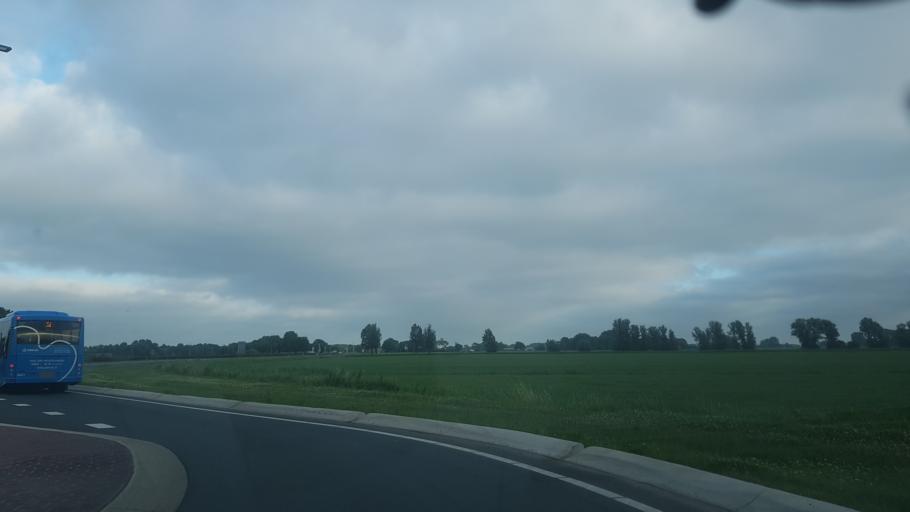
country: NL
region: Friesland
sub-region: Gemeente Leeuwarderadeel
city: Stiens
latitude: 53.2511
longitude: 5.7675
